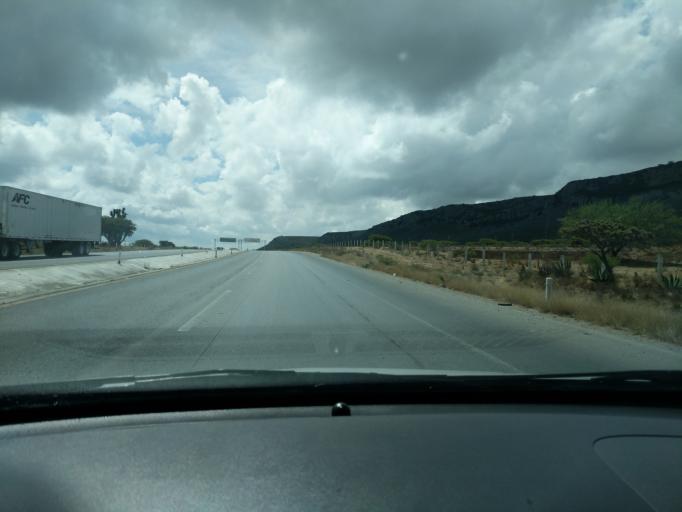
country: MX
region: Zacatecas
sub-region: Pinos
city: Santiago
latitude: 22.4026
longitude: -101.3824
